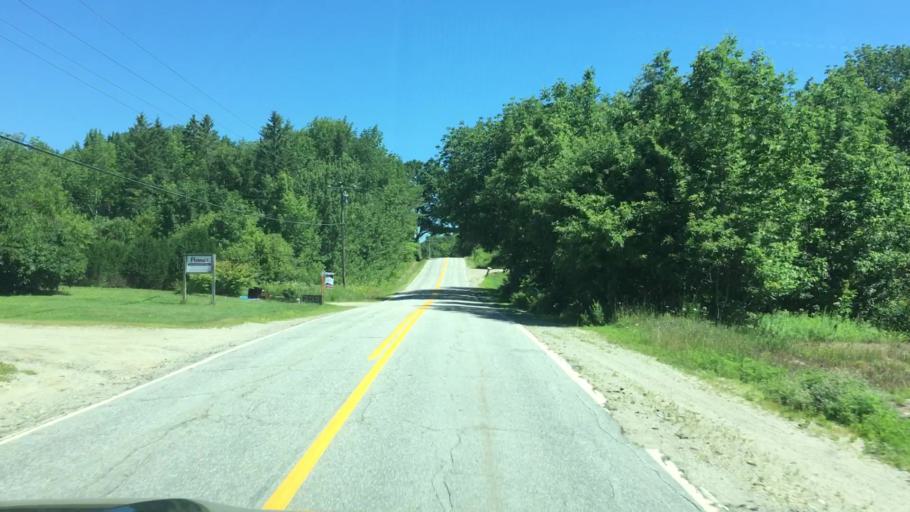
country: US
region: Maine
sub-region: Hancock County
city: Penobscot
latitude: 44.5139
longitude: -68.6718
